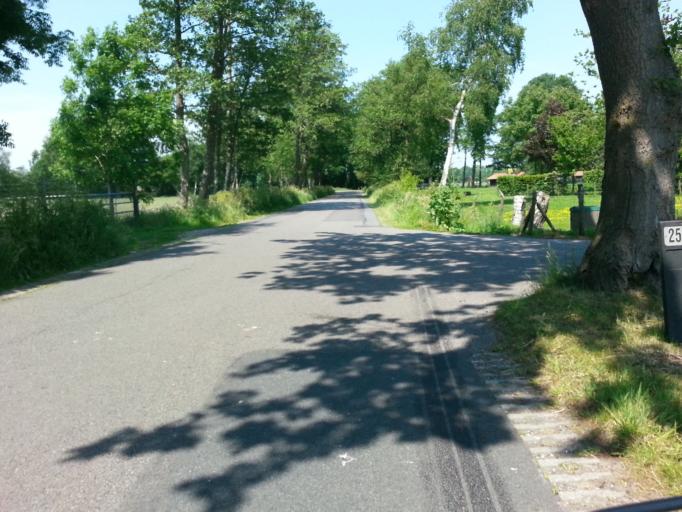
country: NL
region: Gelderland
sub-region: Gemeente Barneveld
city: Terschuur
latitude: 52.1227
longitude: 5.5307
